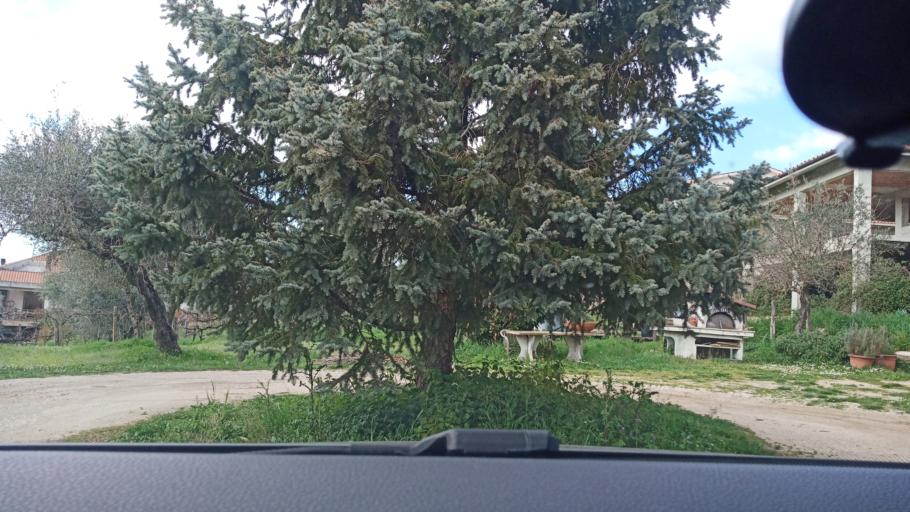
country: IT
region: Latium
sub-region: Provincia di Rieti
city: Stimigliano
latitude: 42.3028
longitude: 12.5638
